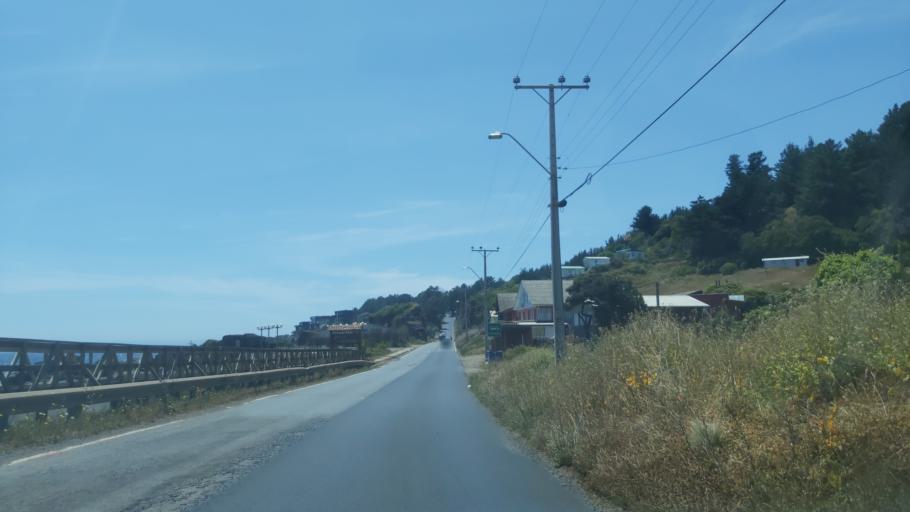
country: CL
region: Maule
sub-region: Provincia de Cauquenes
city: Cauquenes
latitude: -35.8375
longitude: -72.6255
